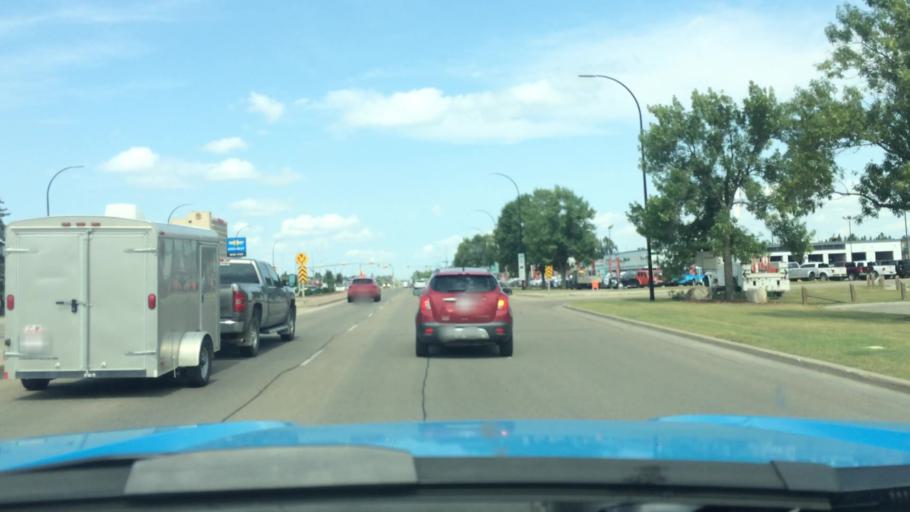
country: CA
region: Alberta
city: Red Deer
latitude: 52.2485
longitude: -113.8139
